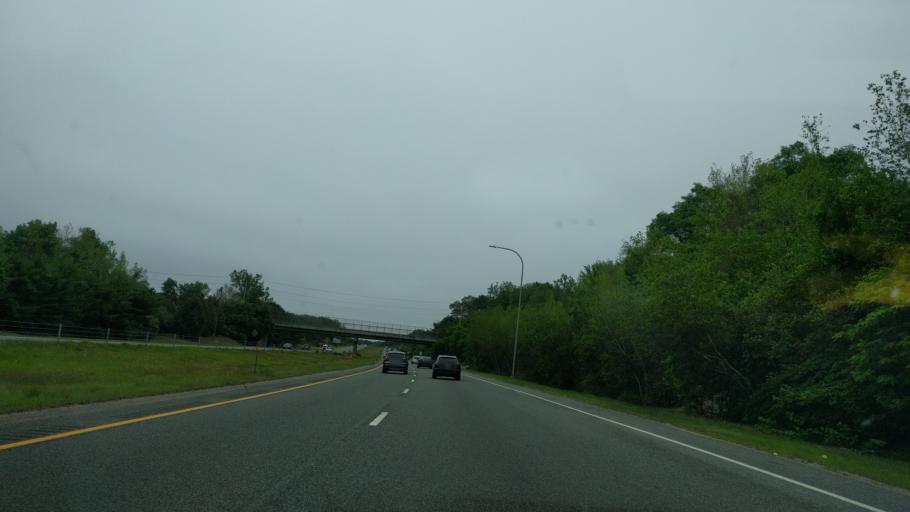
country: US
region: Rhode Island
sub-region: Washington County
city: Exeter
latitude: 41.6101
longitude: -71.4957
